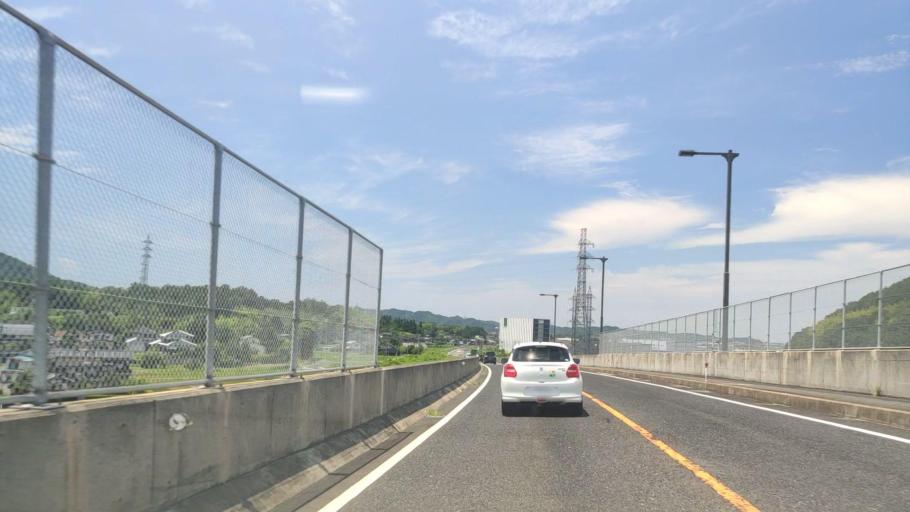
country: JP
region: Tottori
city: Tottori
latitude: 35.4489
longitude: 134.2534
